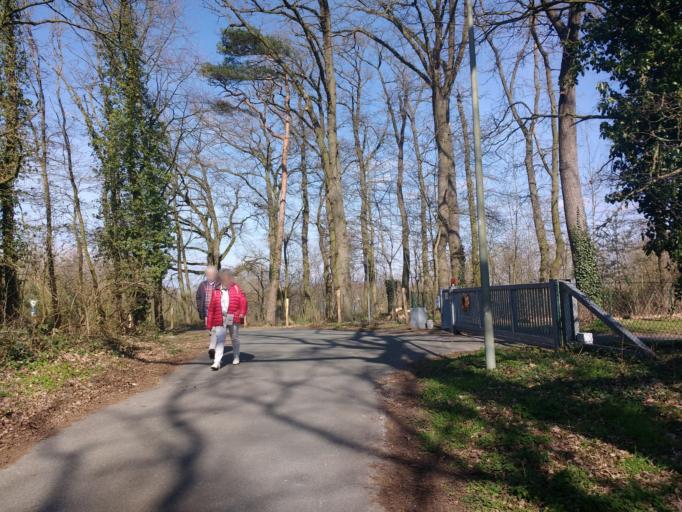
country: DE
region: North Rhine-Westphalia
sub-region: Regierungsbezirk Detmold
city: Hovelhof
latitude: 51.7533
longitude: 8.6769
